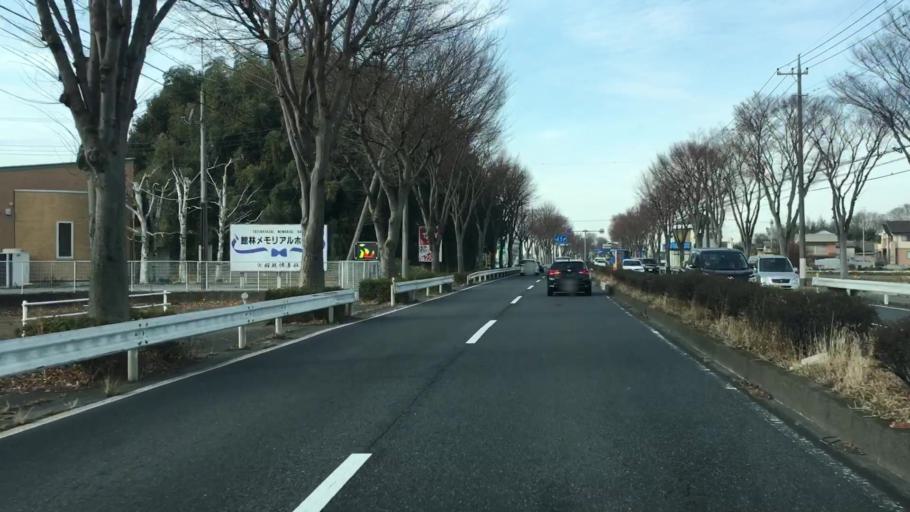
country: JP
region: Gunma
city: Tatebayashi
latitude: 36.2304
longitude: 139.5598
